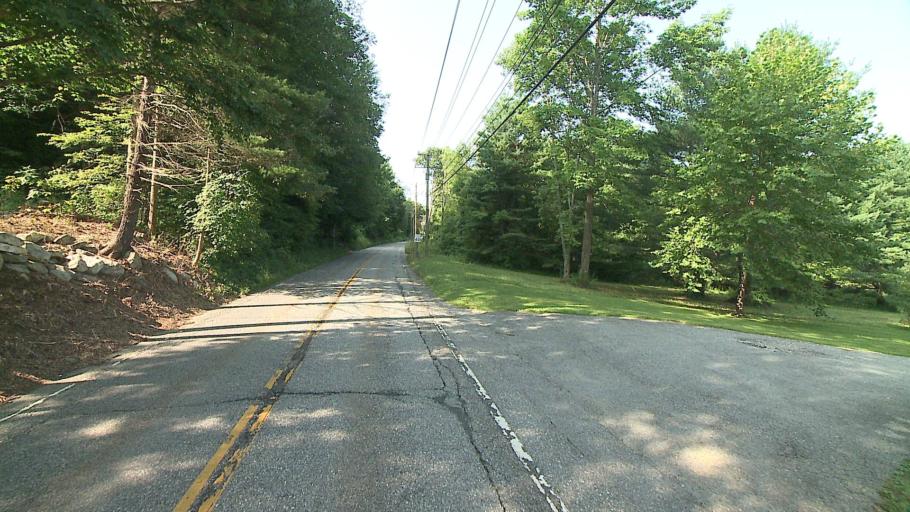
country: US
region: Connecticut
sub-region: Litchfield County
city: Kent
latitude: 41.7957
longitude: -73.3952
